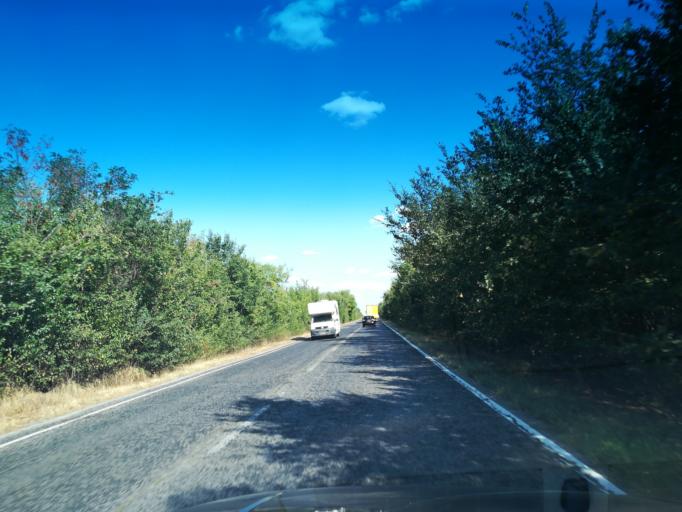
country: BG
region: Khaskovo
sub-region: Obshtina Mineralni Bani
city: Mineralni Bani
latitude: 42.0538
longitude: 25.3143
